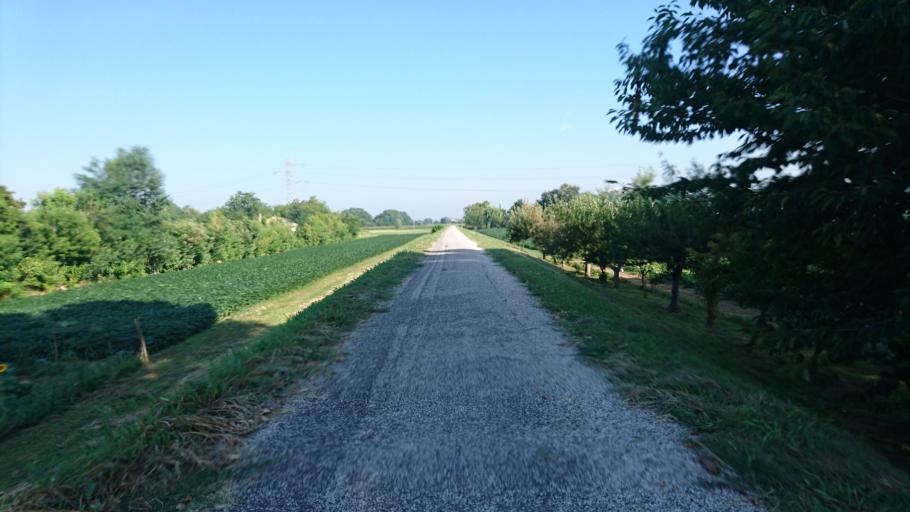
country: IT
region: Veneto
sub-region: Provincia di Padova
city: Cervarese Santa Croce
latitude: 45.4332
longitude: 11.6860
